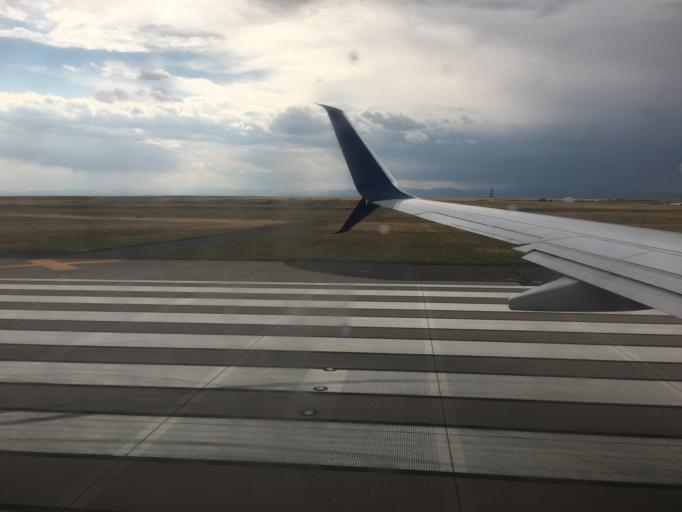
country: US
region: Colorado
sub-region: Weld County
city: Lochbuie
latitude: 39.8523
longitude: -104.6966
